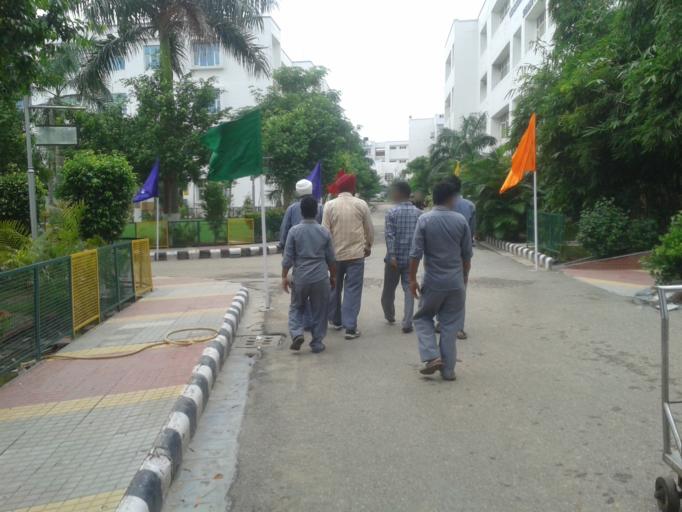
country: IN
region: Punjab
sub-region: Ajitgarh
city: Mohali
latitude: 30.6864
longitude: 76.6643
